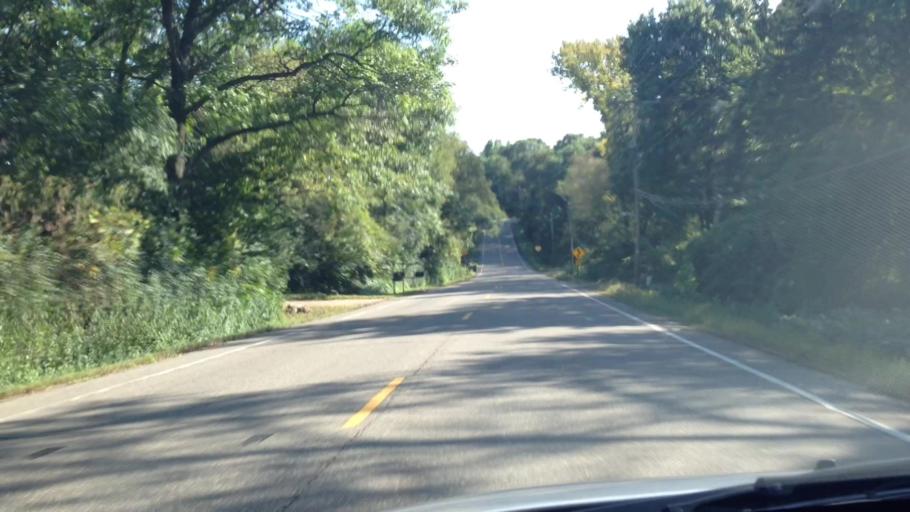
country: US
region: Minnesota
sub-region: Washington County
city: Stillwater
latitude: 45.0855
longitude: -92.8130
